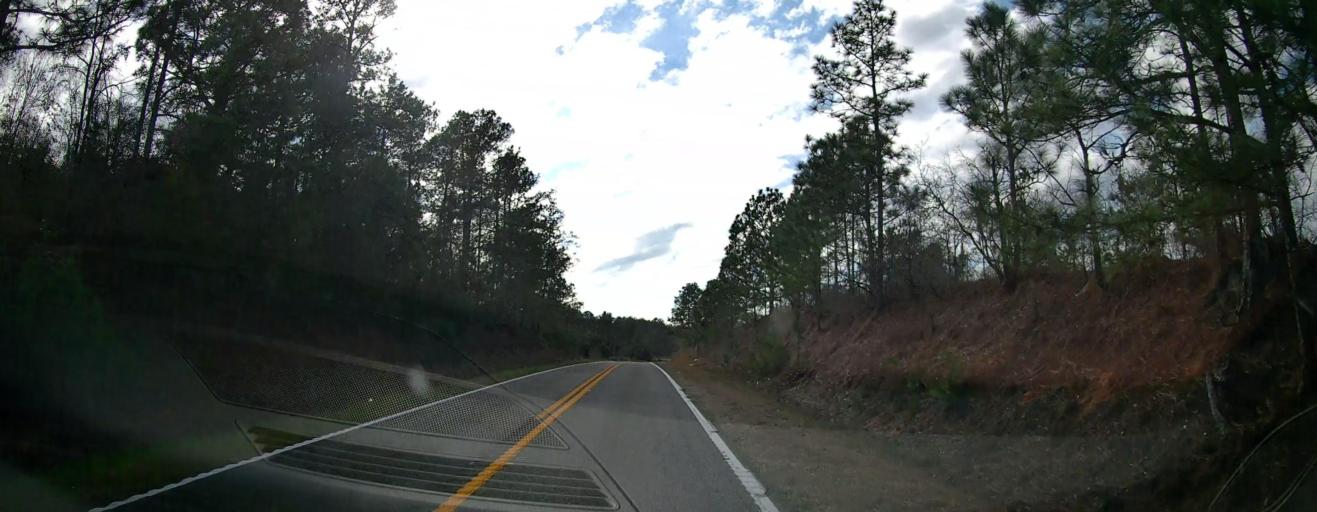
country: US
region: Georgia
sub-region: Marion County
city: Buena Vista
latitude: 32.4382
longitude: -84.5029
